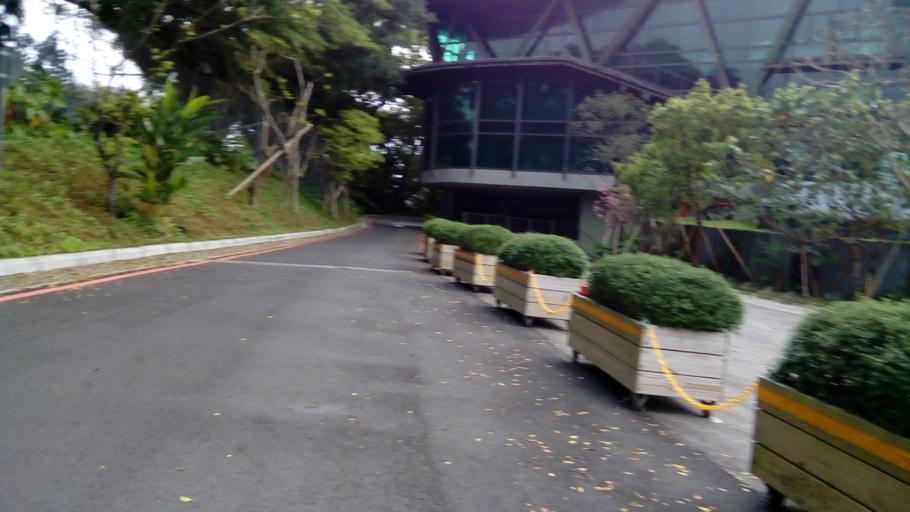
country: TW
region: Taipei
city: Taipei
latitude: 25.1807
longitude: 121.4286
